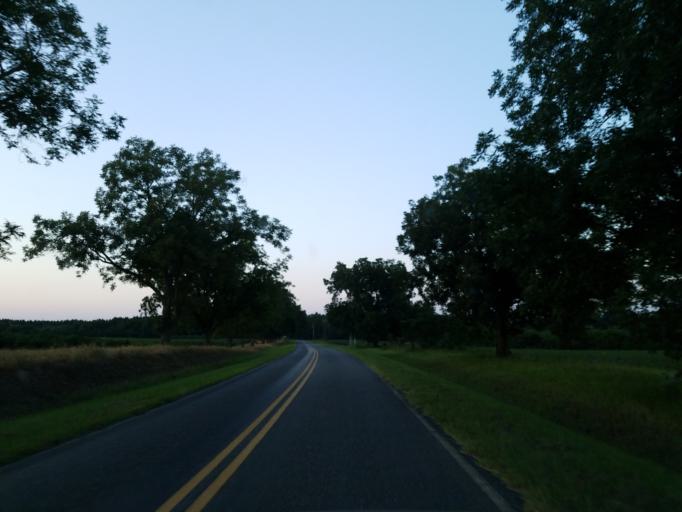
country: US
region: Georgia
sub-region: Dooly County
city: Vienna
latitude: 32.1668
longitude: -83.7985
